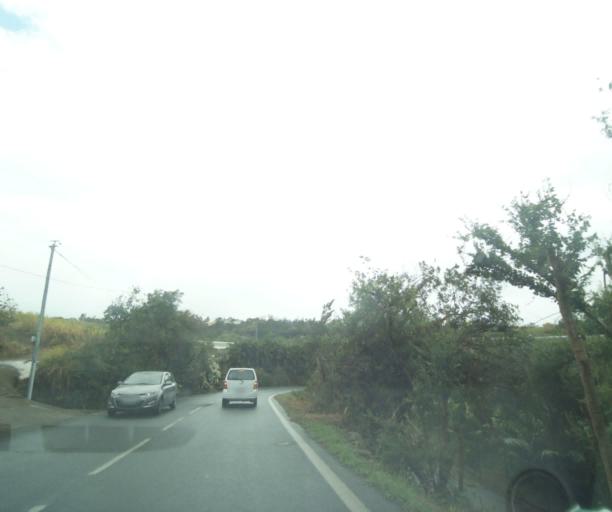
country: RE
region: Reunion
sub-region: Reunion
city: Saint-Paul
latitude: -21.0339
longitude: 55.2816
